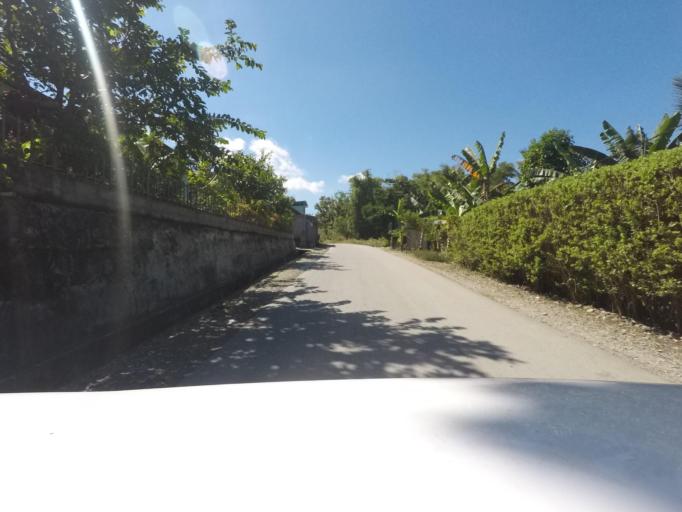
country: TL
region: Ermera
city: Gleno
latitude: -8.7122
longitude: 125.4451
